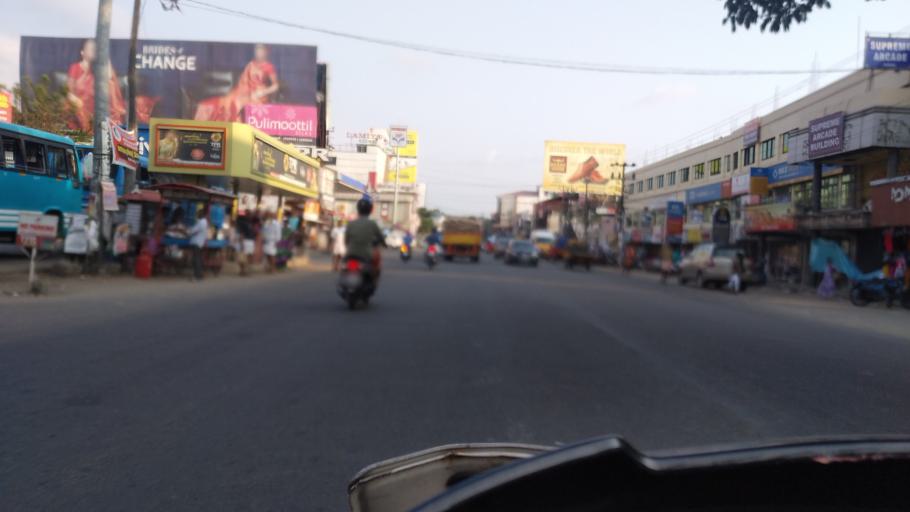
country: IN
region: Kerala
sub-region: Thrissur District
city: Thanniyam
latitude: 10.4150
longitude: 76.1072
